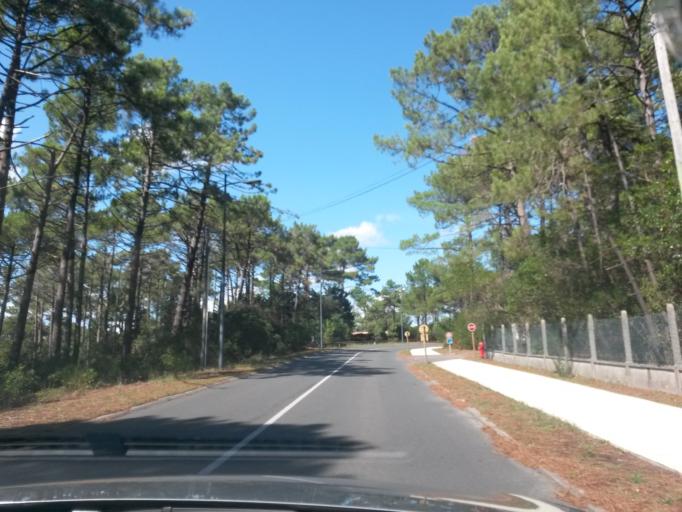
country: FR
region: Aquitaine
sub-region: Departement de la Gironde
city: Arcachon
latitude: 44.6819
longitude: -1.2393
